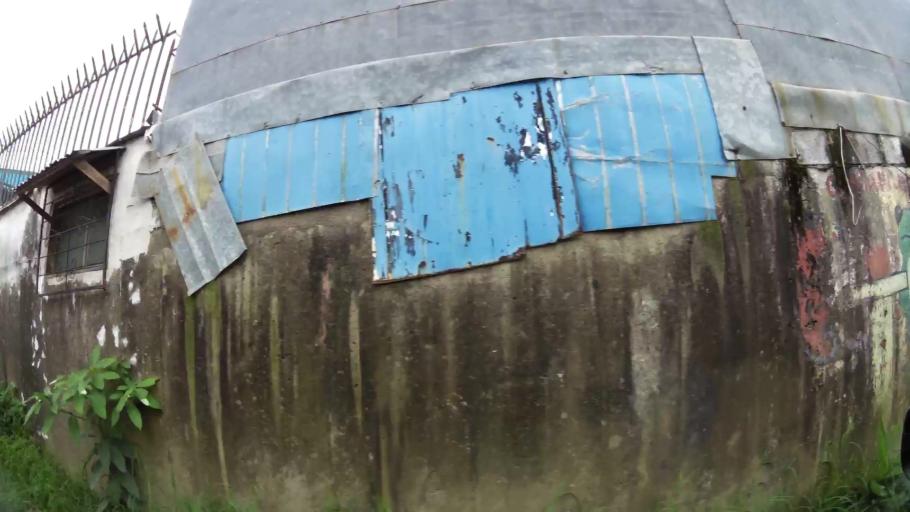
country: CR
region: San Jose
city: Curridabat
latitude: 9.9221
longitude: -84.0392
